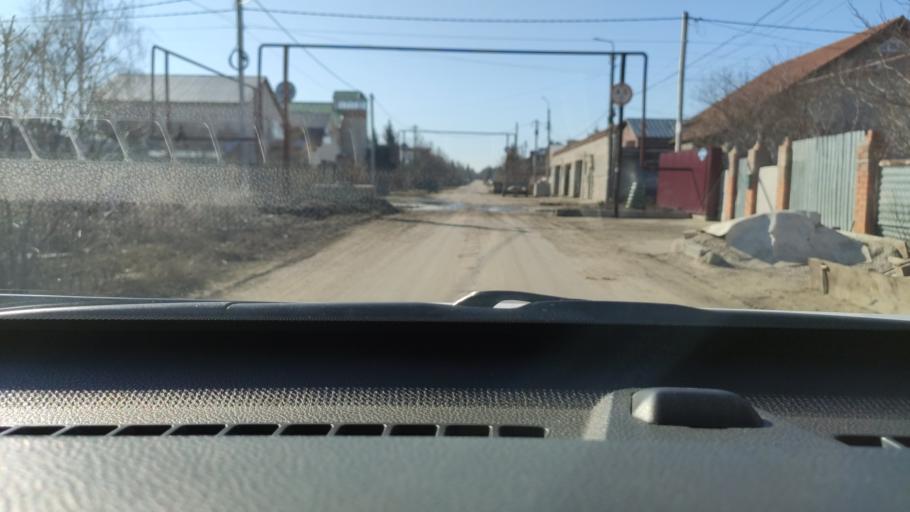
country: RU
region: Samara
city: Tol'yatti
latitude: 53.5671
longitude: 49.3880
